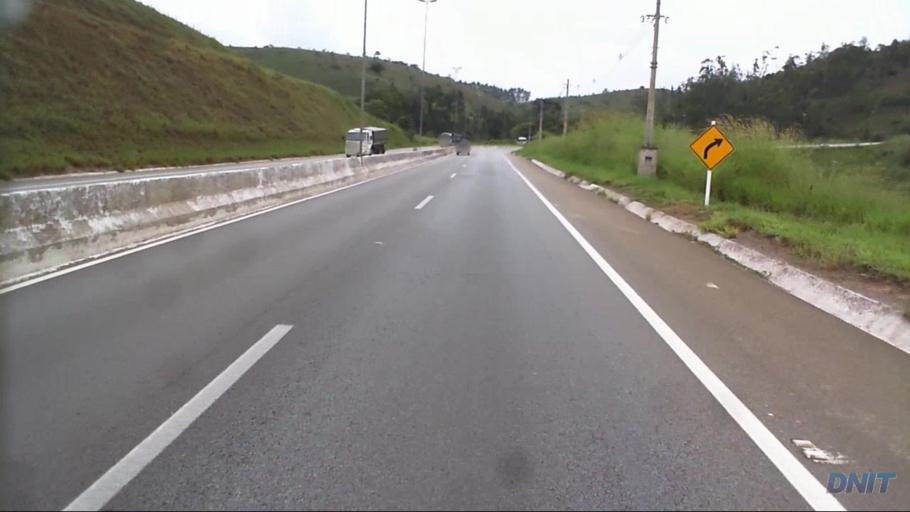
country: BR
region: Minas Gerais
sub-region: Nova Era
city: Nova Era
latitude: -19.7645
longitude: -43.0476
